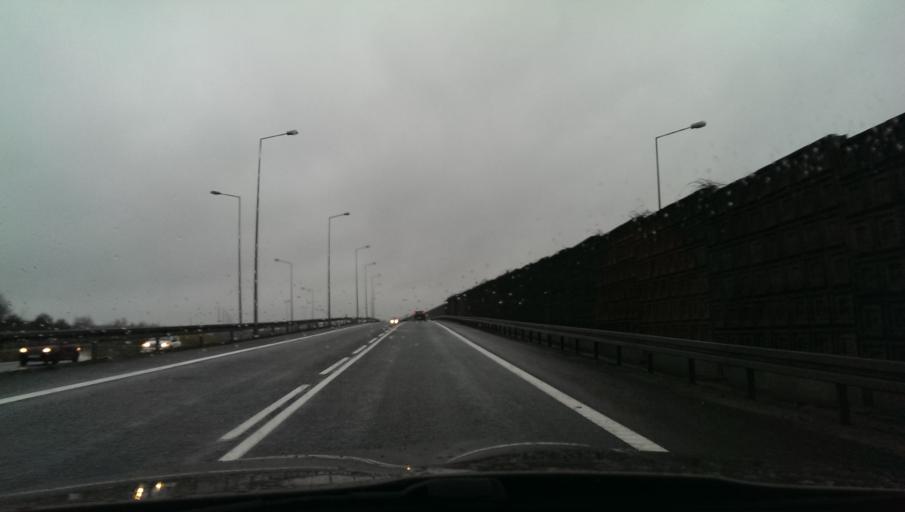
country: PL
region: Subcarpathian Voivodeship
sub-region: Powiat rzeszowski
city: Glogow Malopolski
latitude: 50.1406
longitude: 21.9644
